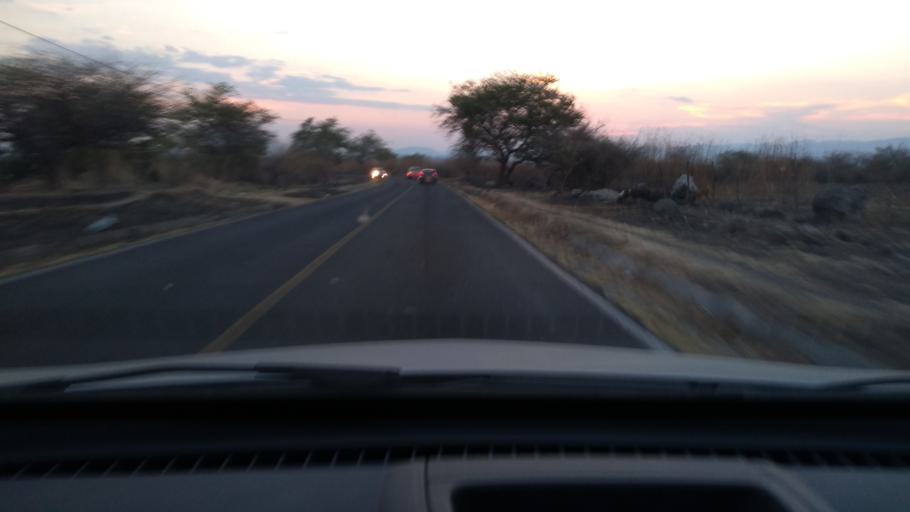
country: MX
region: Morelos
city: Coatetelco
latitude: 18.7245
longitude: -99.2995
